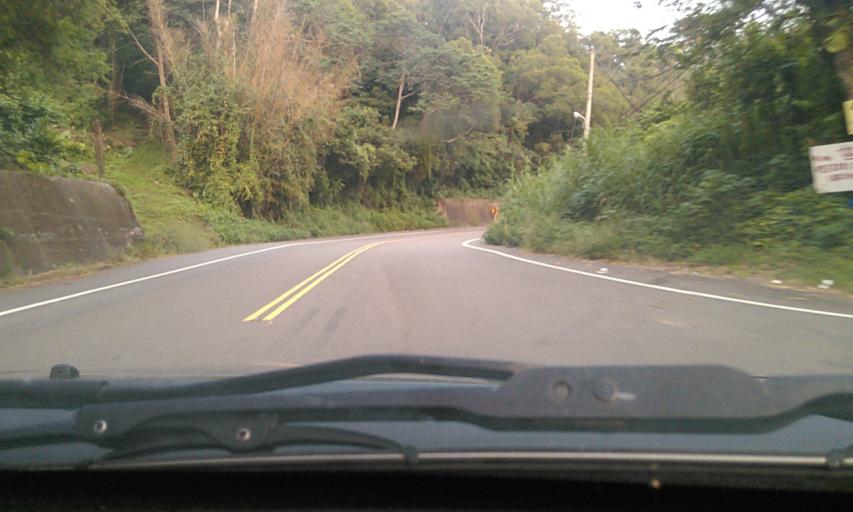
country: TW
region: Taiwan
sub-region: Hsinchu
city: Hsinchu
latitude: 24.6861
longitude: 120.9784
